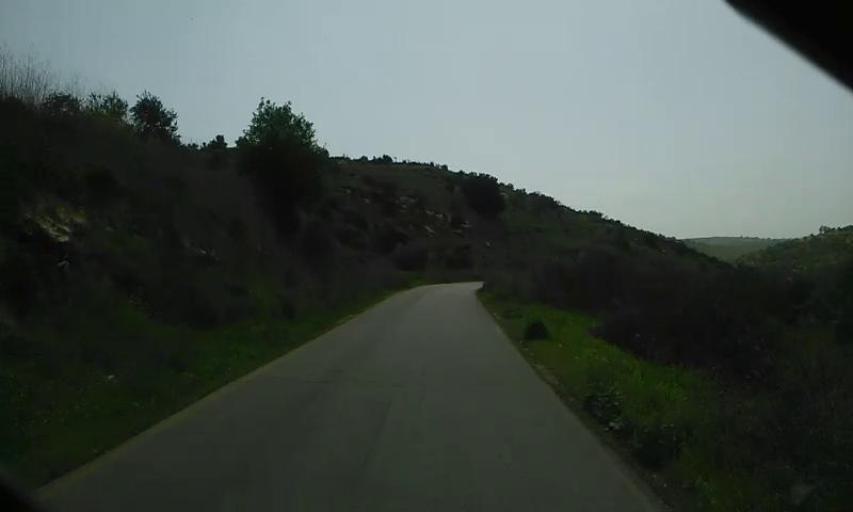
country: PS
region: West Bank
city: Silat al Harithiyah
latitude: 32.5134
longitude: 35.2141
